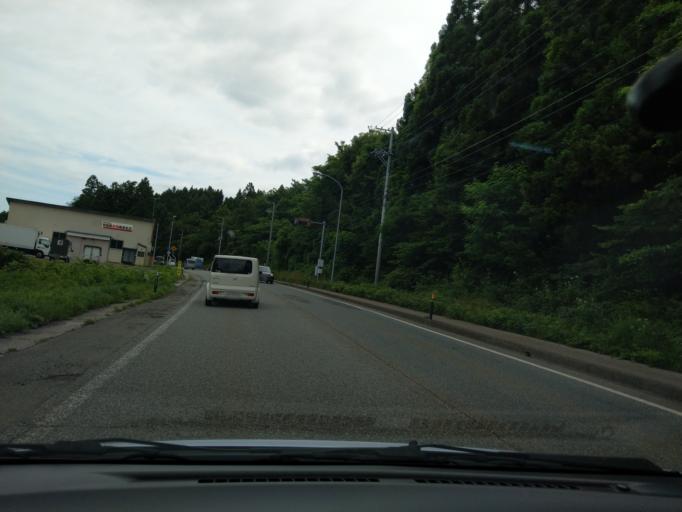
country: JP
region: Akita
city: Yokotemachi
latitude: 39.3365
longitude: 140.5606
